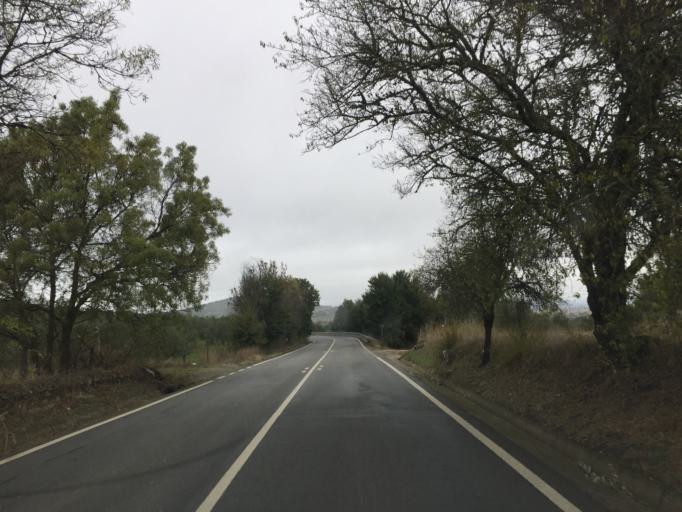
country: PT
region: Portalegre
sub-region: Alter do Chao
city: Alter do Chao
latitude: 39.2118
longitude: -7.6559
